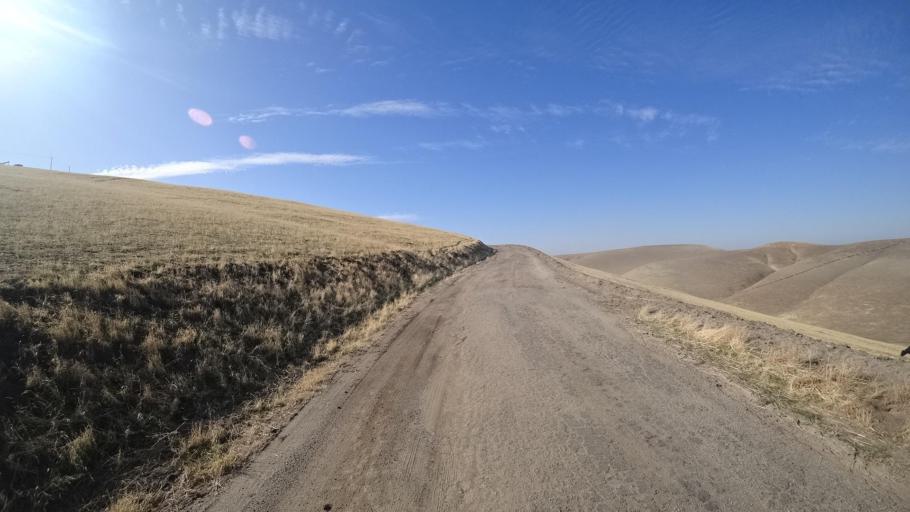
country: US
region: California
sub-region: Kern County
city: Oildale
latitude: 35.4905
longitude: -118.8764
